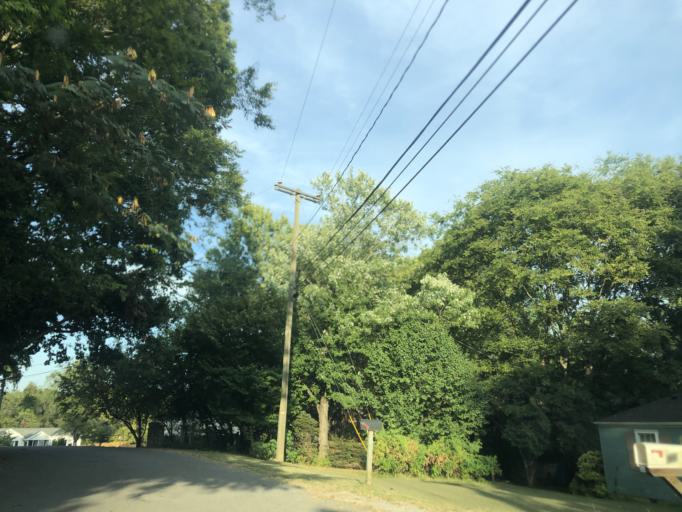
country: US
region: Tennessee
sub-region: Davidson County
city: Oak Hill
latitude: 36.1229
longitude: -86.7396
